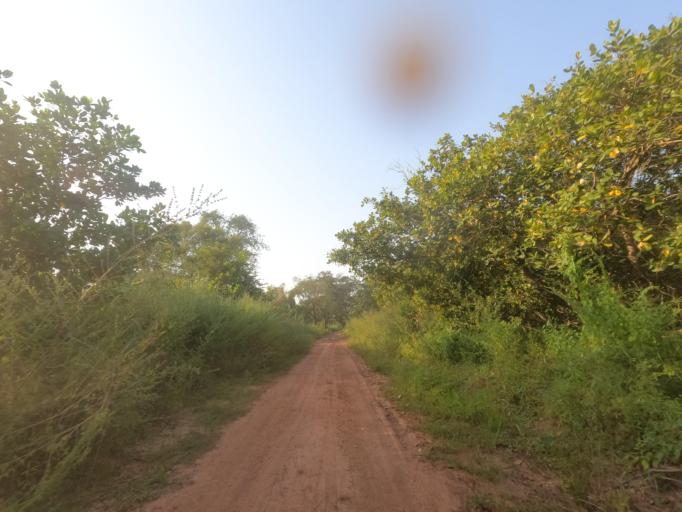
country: GW
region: Oio
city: Bissora
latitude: 12.3815
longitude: -15.7143
